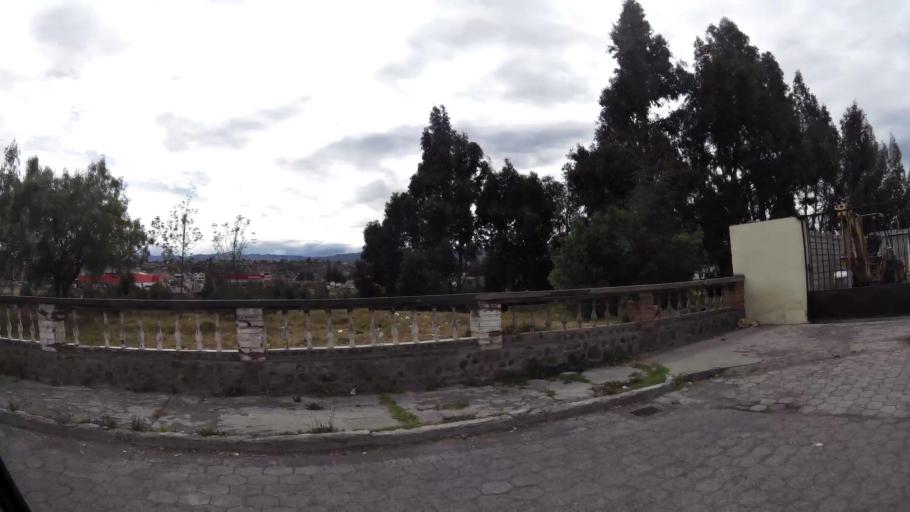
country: EC
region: Cotopaxi
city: Latacunga
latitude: -0.9233
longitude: -78.6237
